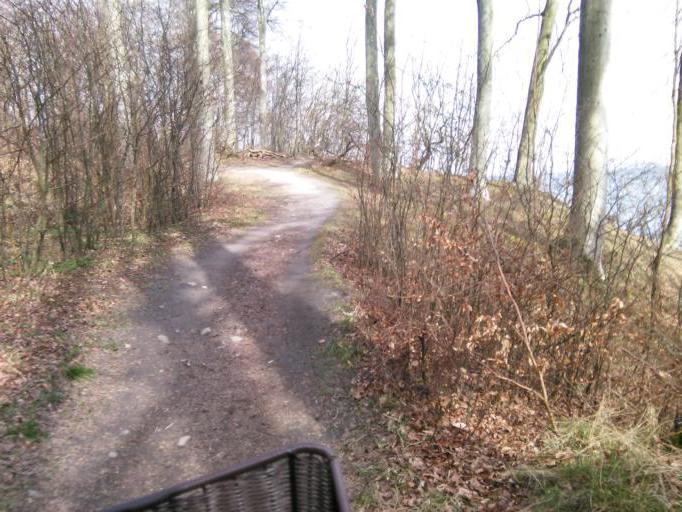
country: DK
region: Central Jutland
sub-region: Arhus Kommune
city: Beder
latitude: 56.0961
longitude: 10.2441
